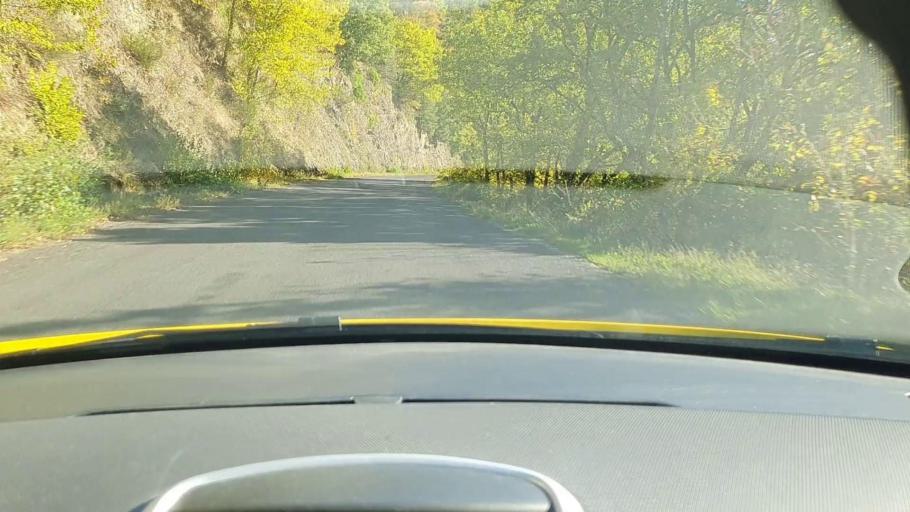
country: FR
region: Languedoc-Roussillon
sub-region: Departement du Gard
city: Le Vigan
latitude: 43.9818
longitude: 3.4945
